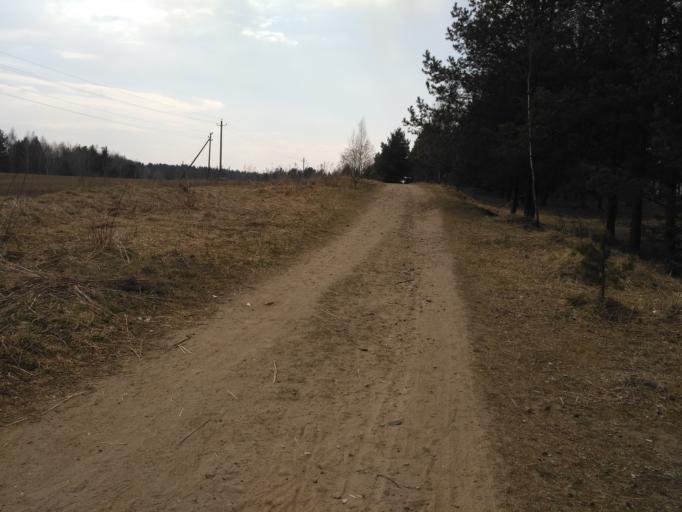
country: BY
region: Minsk
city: Zamostochcha
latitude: 53.8803
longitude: 27.9107
